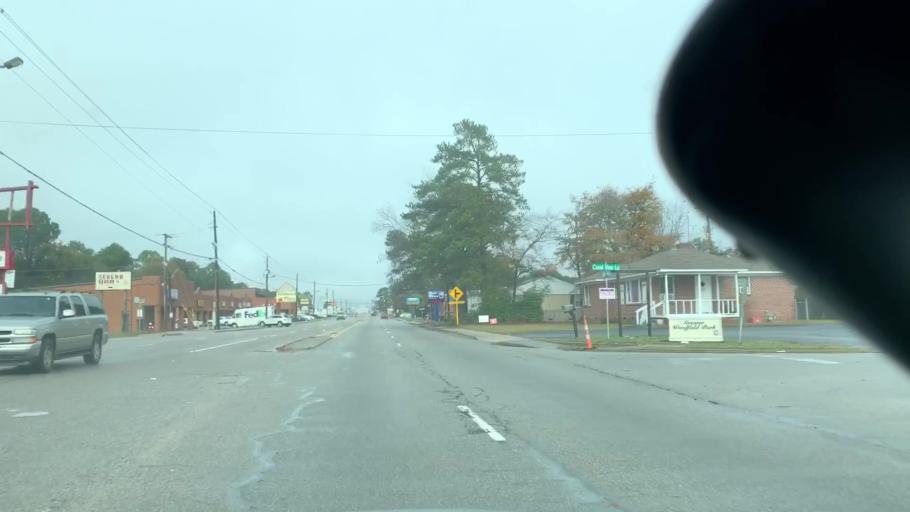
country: US
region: South Carolina
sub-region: Richland County
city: Woodfield
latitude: 34.0456
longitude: -80.9426
